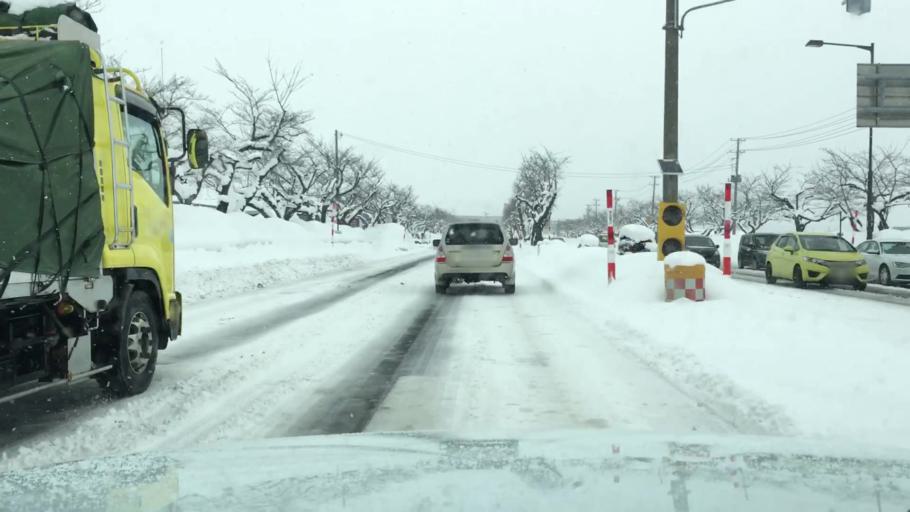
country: JP
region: Aomori
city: Hirosaki
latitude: 40.6369
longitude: 140.4889
